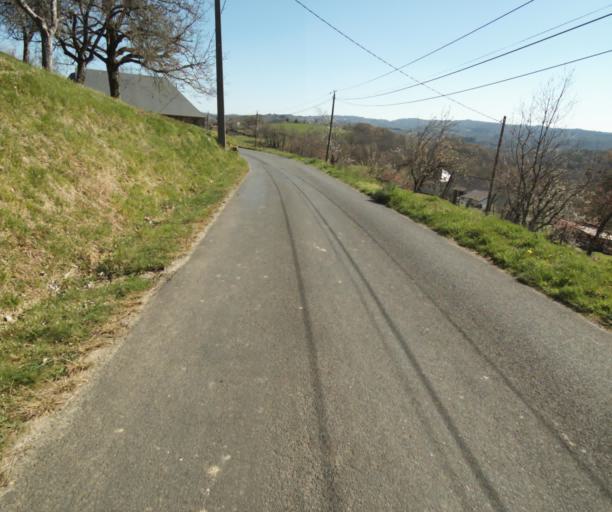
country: FR
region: Limousin
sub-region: Departement de la Correze
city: Chameyrat
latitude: 45.2557
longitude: 1.7261
